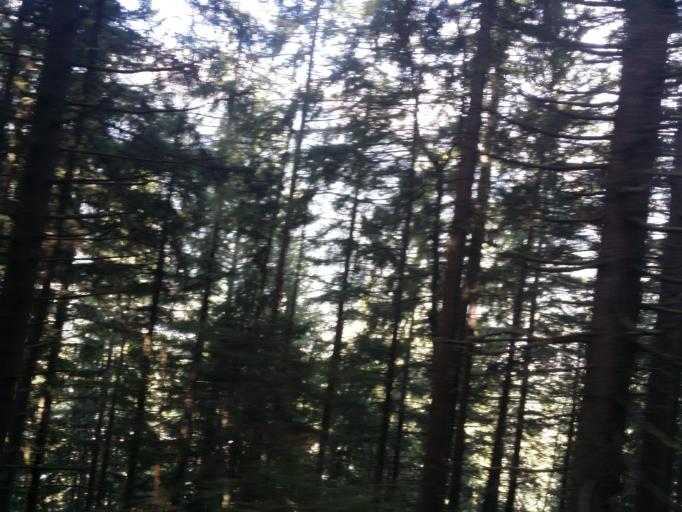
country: FR
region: Rhone-Alpes
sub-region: Departement de la Haute-Savoie
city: Chamonix-Mont-Blanc
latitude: 45.9287
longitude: 6.8866
